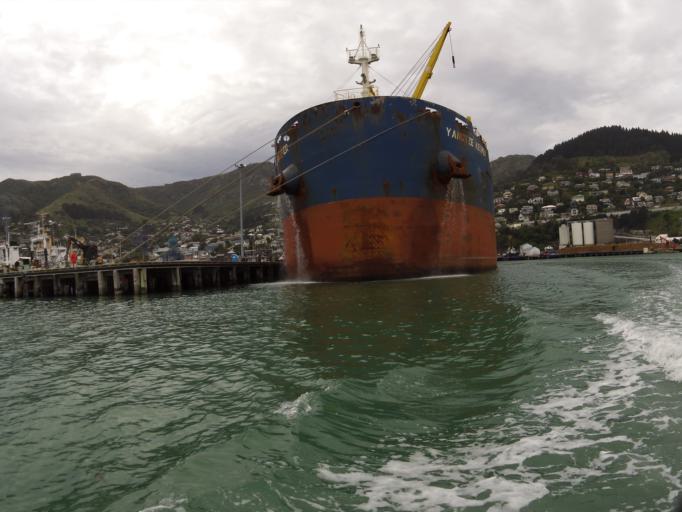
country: NZ
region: Canterbury
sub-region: Christchurch City
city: Christchurch
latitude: -43.6074
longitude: 172.7203
